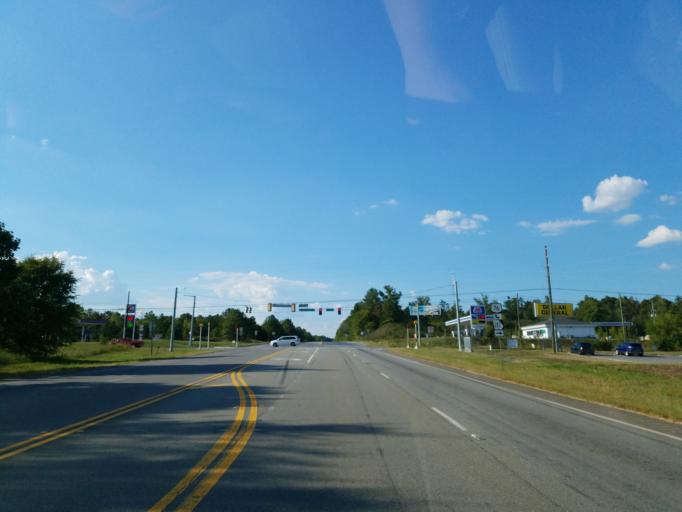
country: US
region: Georgia
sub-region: Murray County
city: Chatsworth
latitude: 34.6960
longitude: -84.7376
